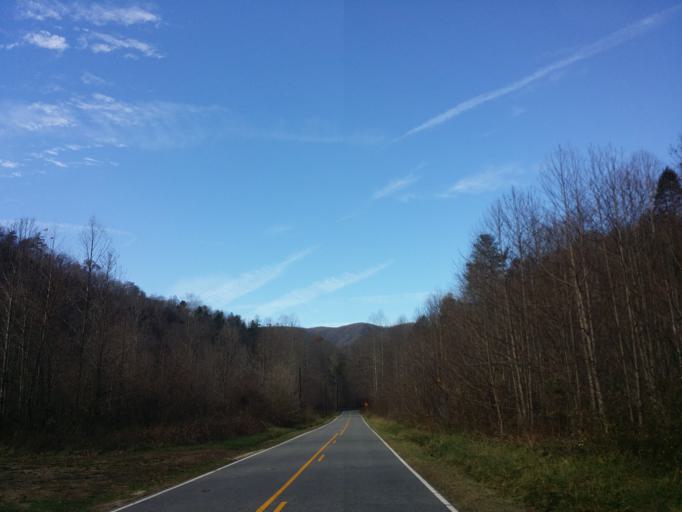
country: US
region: North Carolina
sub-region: McDowell County
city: West Marion
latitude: 35.7379
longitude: -82.1390
